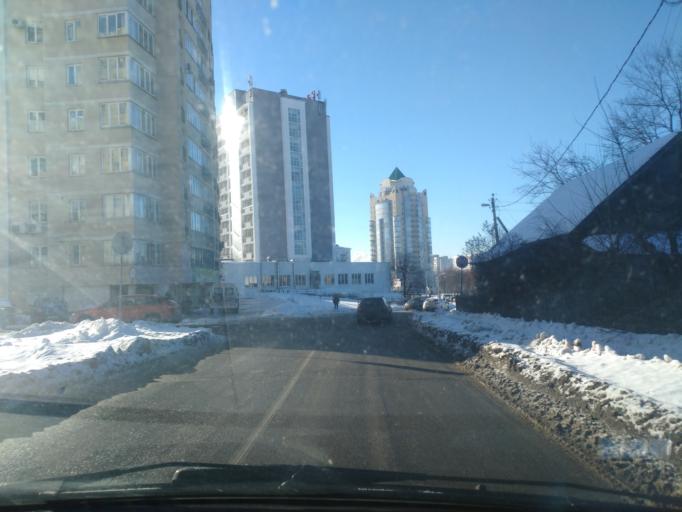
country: BY
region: Mogilev
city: Mahilyow
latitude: 53.9112
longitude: 30.3340
